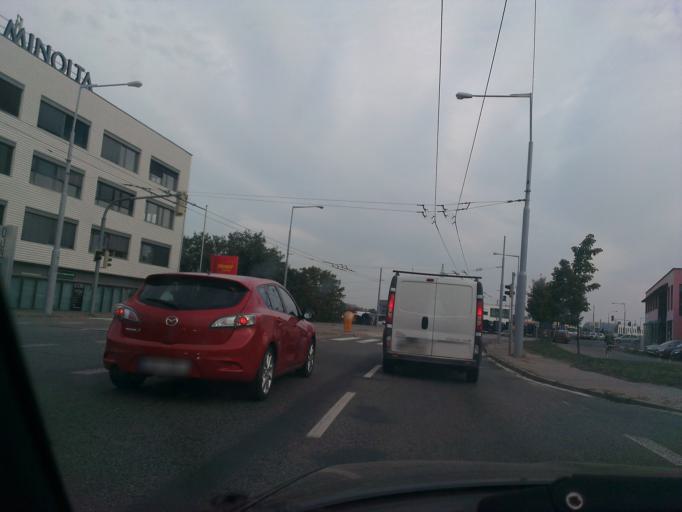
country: CZ
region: South Moravian
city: Bilovice nad Svitavou
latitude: 49.2103
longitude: 16.6623
